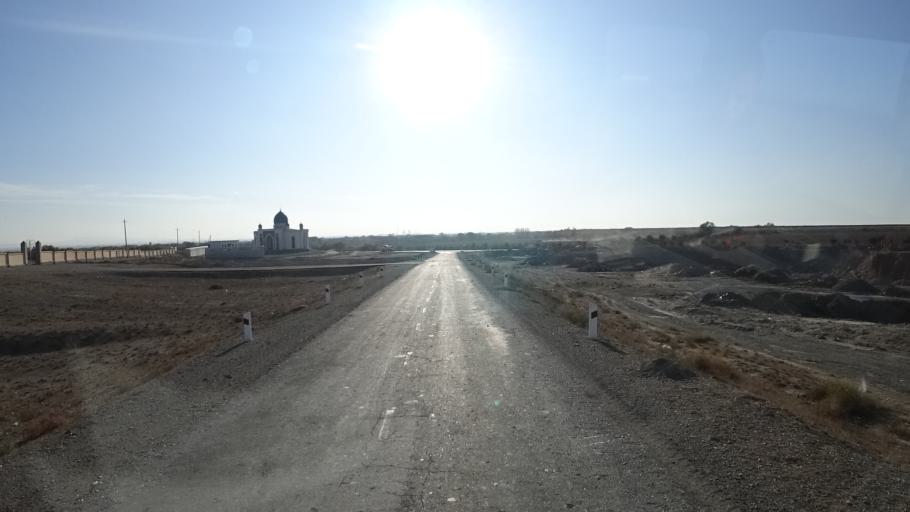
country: UZ
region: Navoiy
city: Beshrabot
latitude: 40.2197
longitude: 65.3853
